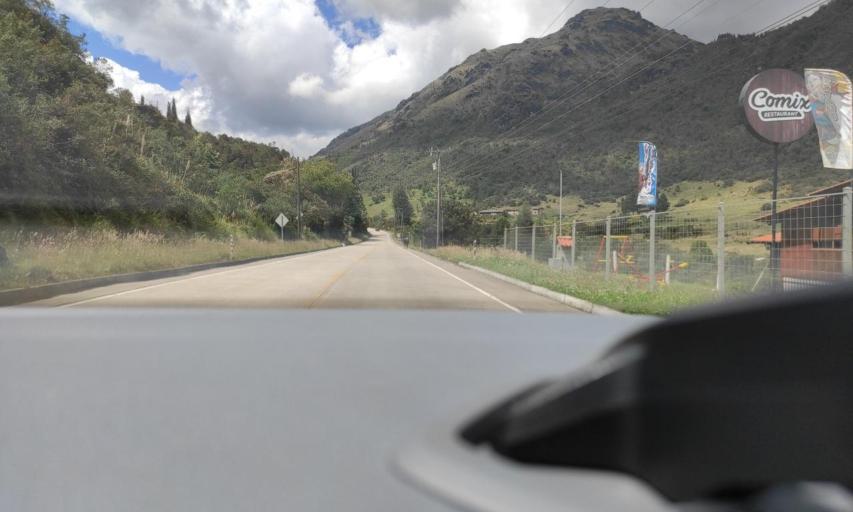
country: EC
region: Azuay
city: Cuenca
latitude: -2.8164
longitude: -79.1494
